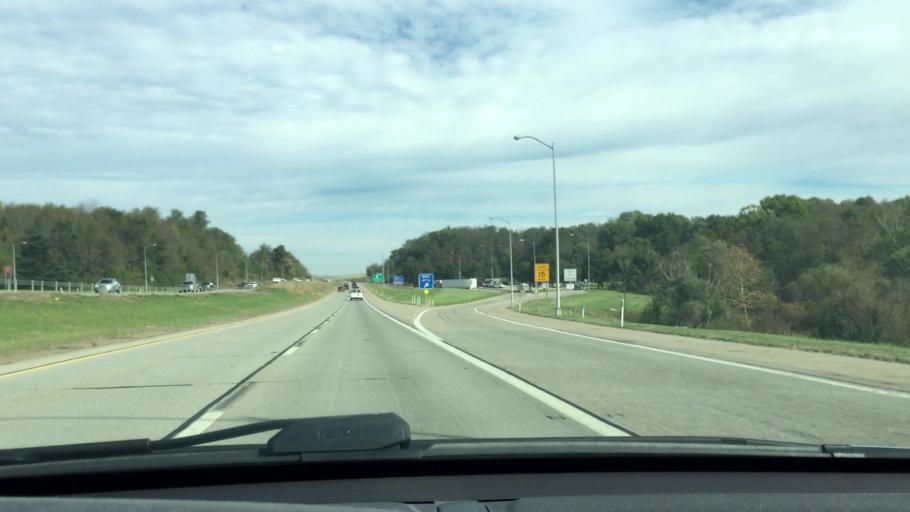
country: US
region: Pennsylvania
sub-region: Allegheny County
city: Bridgeville
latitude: 40.3290
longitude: -80.1399
